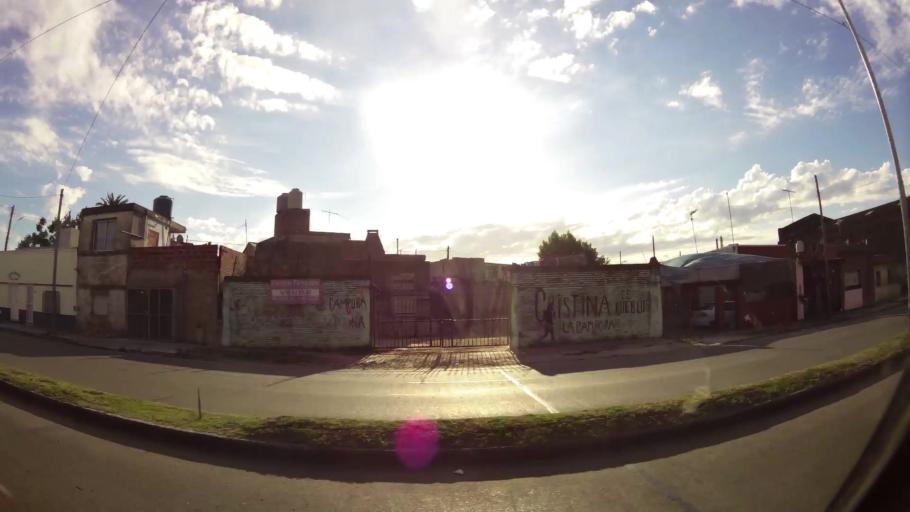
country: AR
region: Buenos Aires
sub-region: Partido de Lanus
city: Lanus
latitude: -34.7014
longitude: -58.3537
